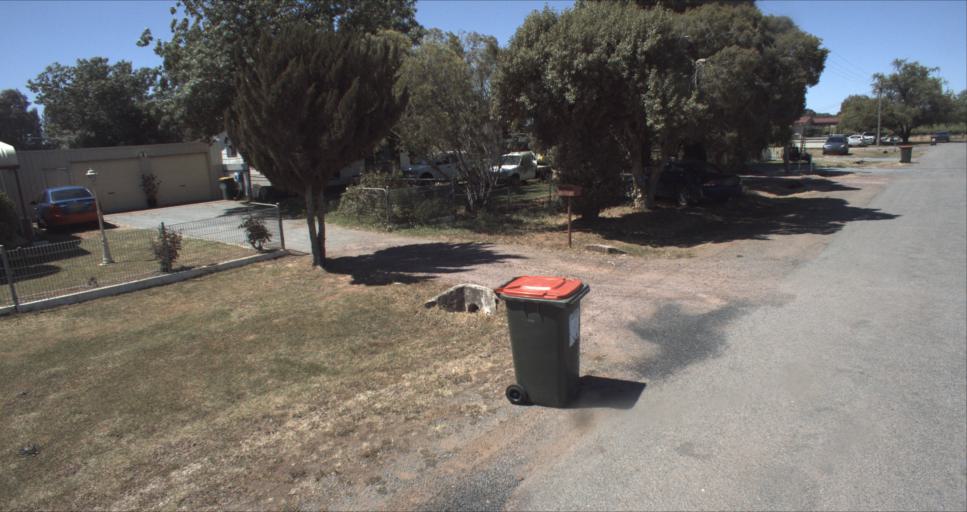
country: AU
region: New South Wales
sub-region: Leeton
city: Leeton
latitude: -34.5239
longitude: 146.3338
